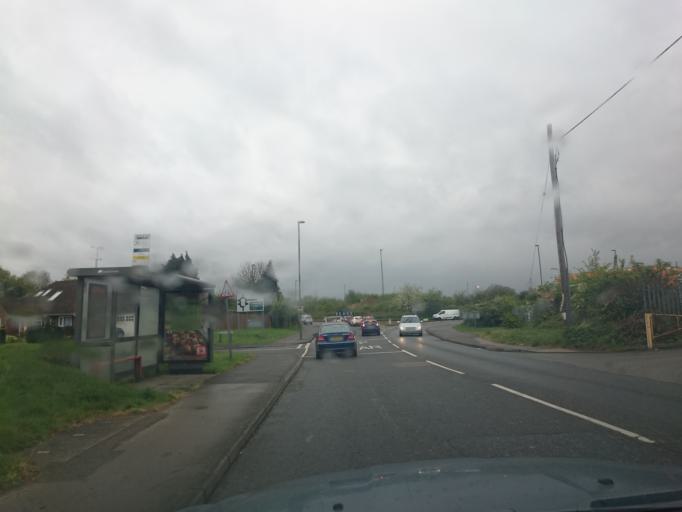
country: GB
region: England
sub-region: Surrey
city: Seale
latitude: 51.2428
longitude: -0.7344
